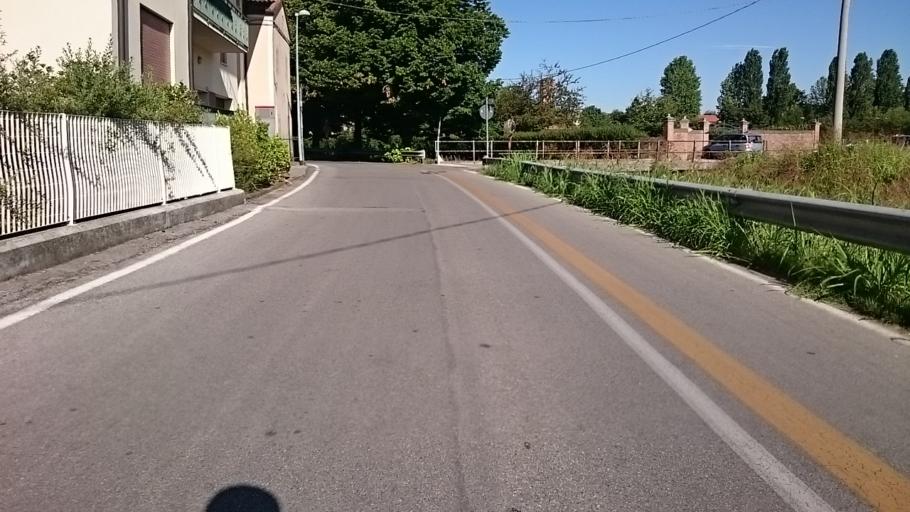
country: IT
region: Veneto
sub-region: Provincia di Padova
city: Camposampiero
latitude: 45.5702
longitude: 11.9361
